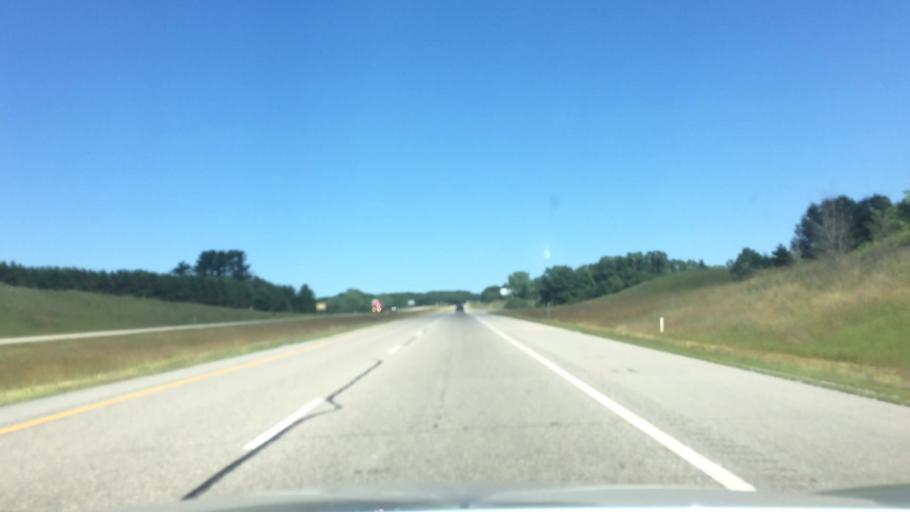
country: US
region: Wisconsin
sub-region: Marquette County
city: Westfield
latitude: 44.0363
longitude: -89.5296
